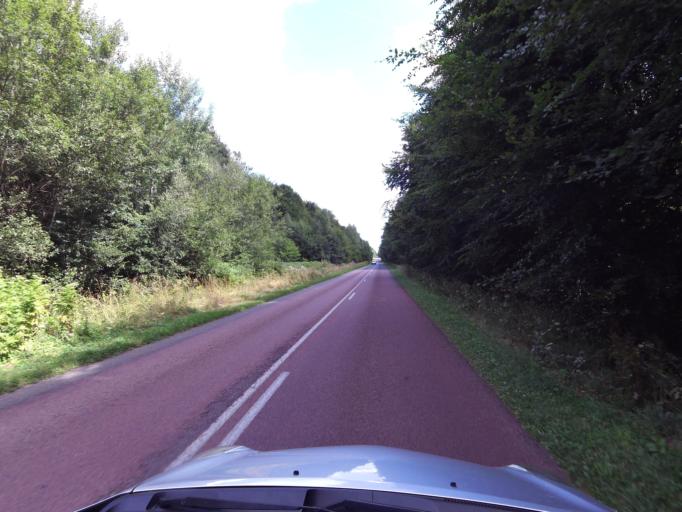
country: FR
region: Picardie
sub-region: Departement de l'Aisne
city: Villers-Cotterets
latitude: 49.2537
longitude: 3.1103
